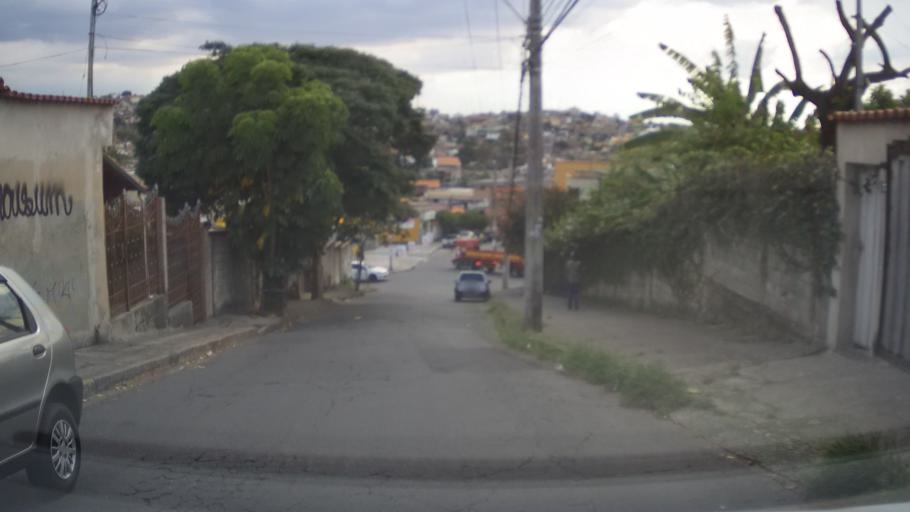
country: BR
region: Minas Gerais
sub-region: Belo Horizonte
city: Belo Horizonte
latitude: -19.8657
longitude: -43.8998
